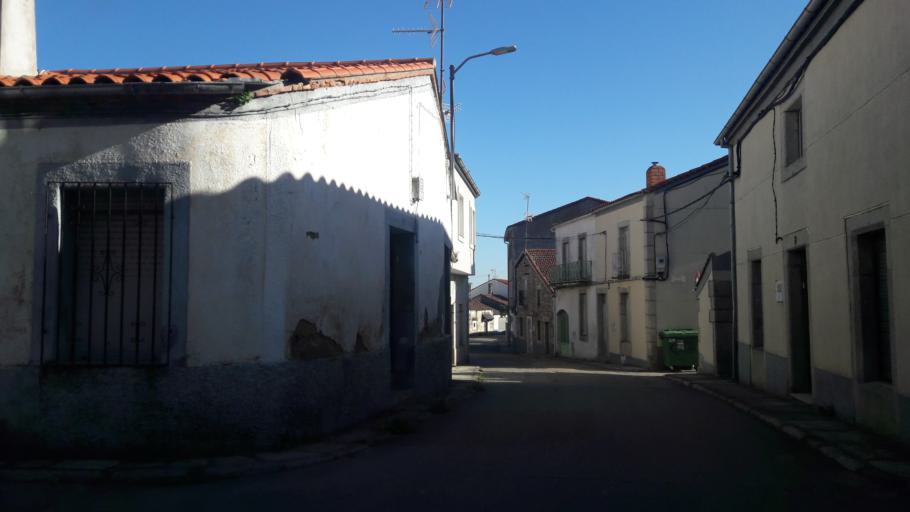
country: ES
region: Castille and Leon
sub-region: Provincia de Salamanca
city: Villavieja de Yeltes
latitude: 40.8766
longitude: -6.4673
